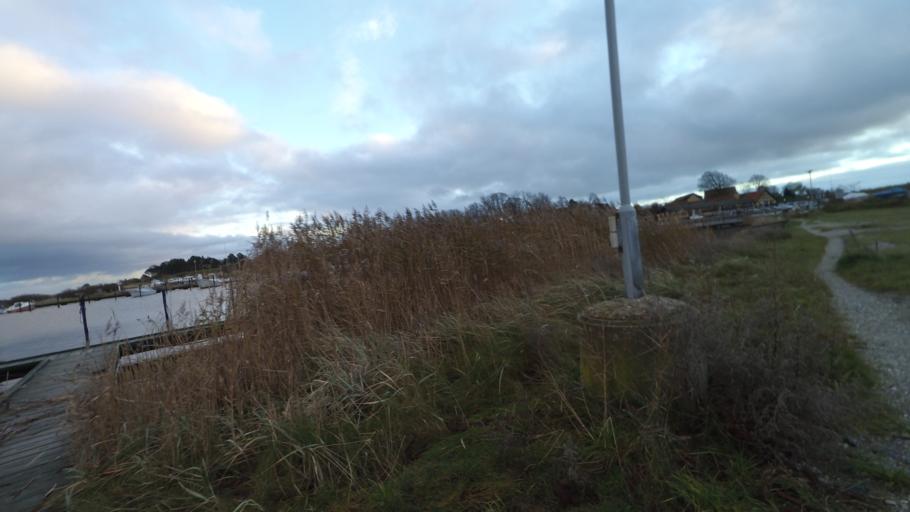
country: DK
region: Central Jutland
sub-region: Arhus Kommune
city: Beder
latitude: 56.0241
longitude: 10.2620
